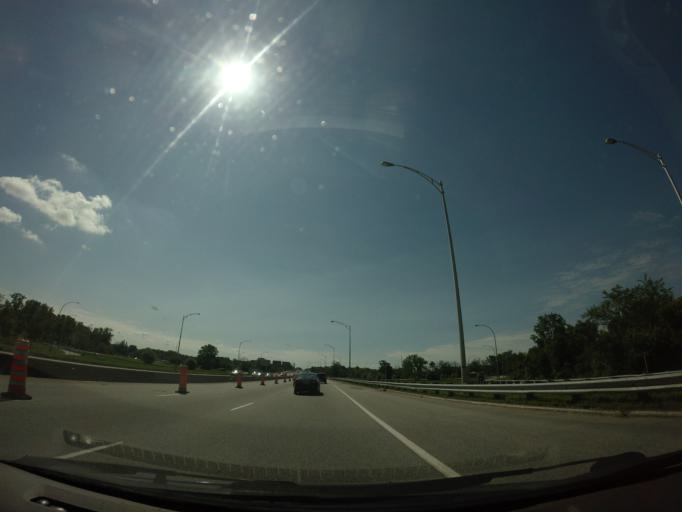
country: CA
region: Quebec
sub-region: Outaouais
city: Gatineau
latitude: 45.4626
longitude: -75.7164
